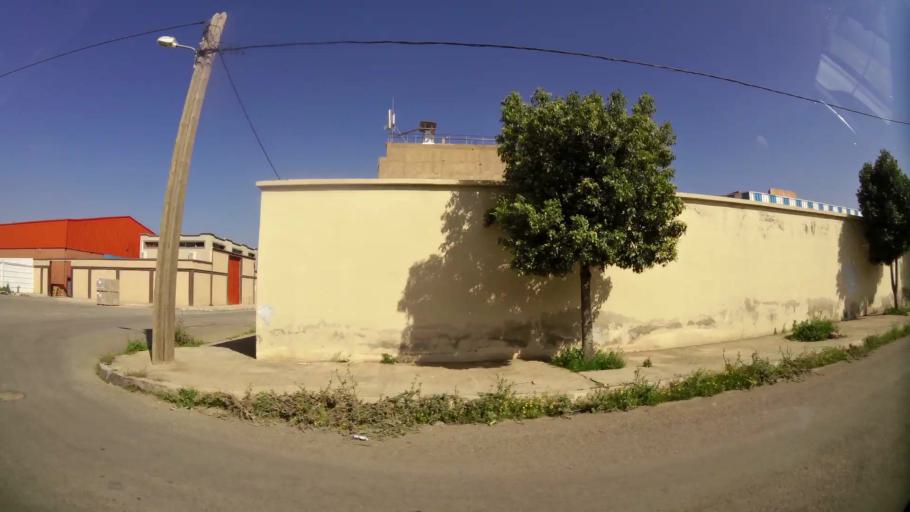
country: MA
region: Oriental
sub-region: Oujda-Angad
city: Oujda
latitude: 34.7056
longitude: -1.8881
